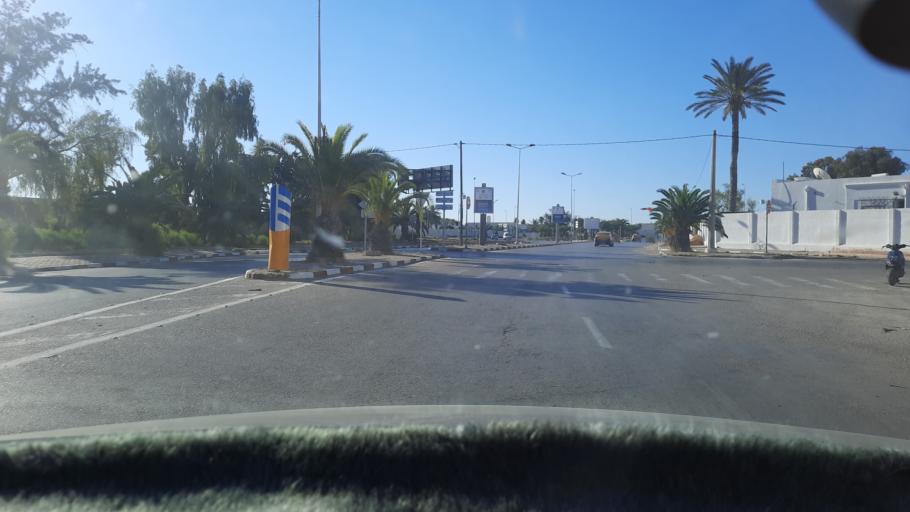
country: TN
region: Safaqis
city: Sfax
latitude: 34.7322
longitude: 10.7450
